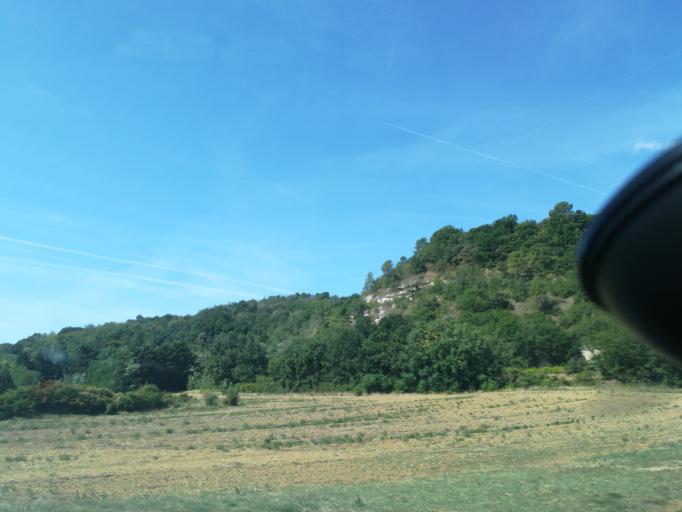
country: FR
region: Rhone-Alpes
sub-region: Departement de la Drome
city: Mours-Saint-Eusebe
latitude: 45.0706
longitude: 5.0304
